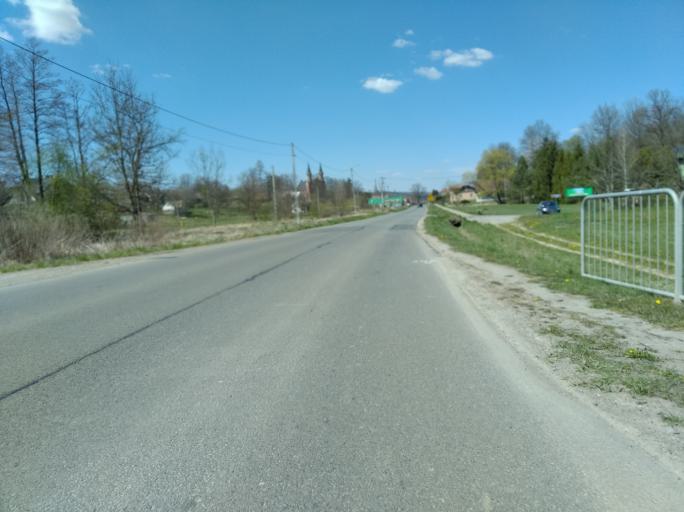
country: PL
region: Subcarpathian Voivodeship
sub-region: Powiat brzozowski
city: Dydnia
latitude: 49.6823
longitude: 22.1822
